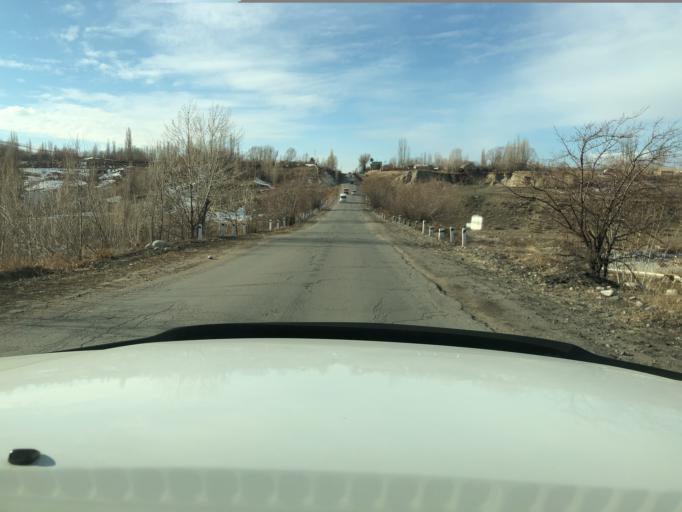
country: KG
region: Ysyk-Koel
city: Pokrovka
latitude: 42.3192
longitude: 77.9040
